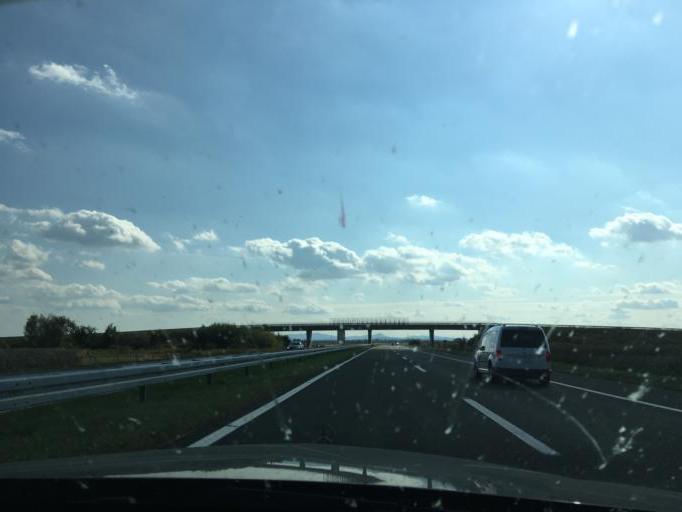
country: HR
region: Medimurska
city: Orehovica
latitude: 46.3424
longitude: 16.5303
